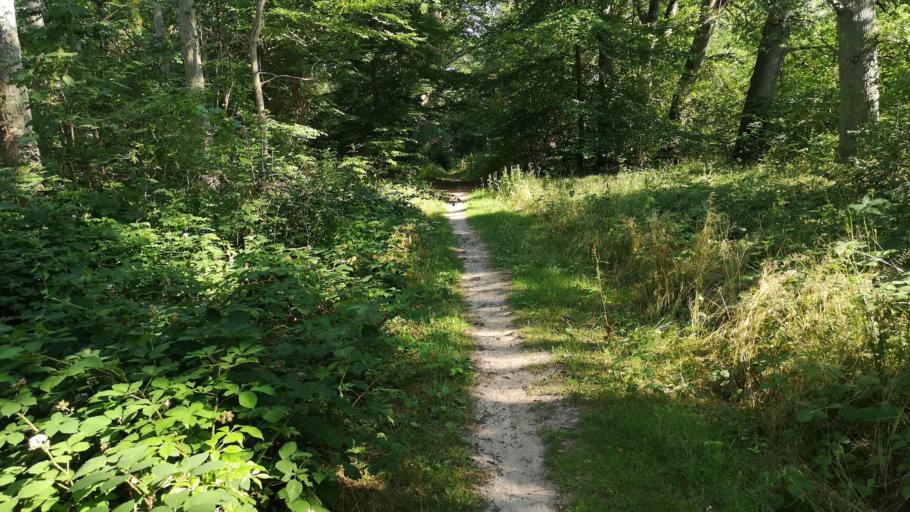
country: DE
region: Lower Saxony
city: Dahlenburg
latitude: 53.2106
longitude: 10.7185
